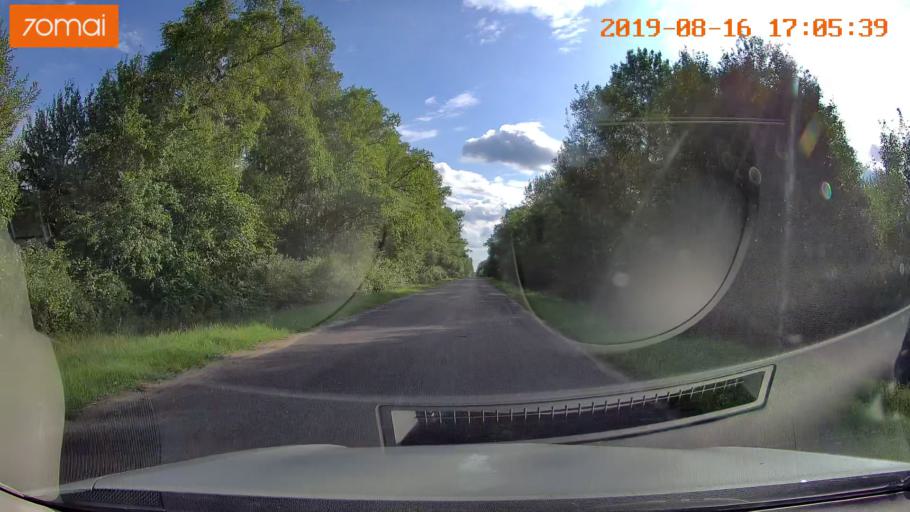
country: BY
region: Mogilev
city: Hlusha
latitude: 53.2354
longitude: 28.9420
